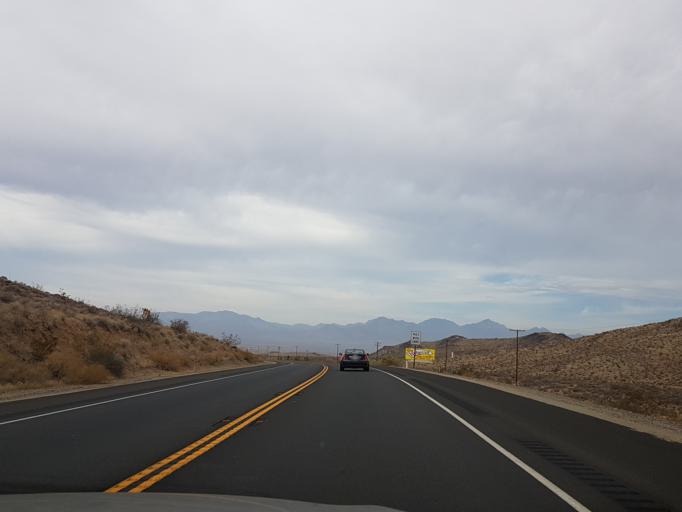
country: US
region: California
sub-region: Kern County
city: Ridgecrest
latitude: 35.5442
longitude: -117.6916
